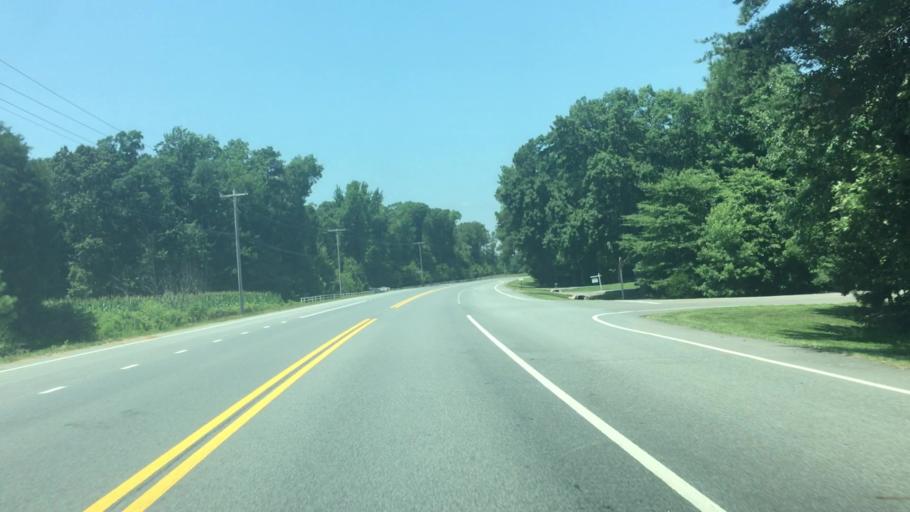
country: US
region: Maryland
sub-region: Saint Mary's County
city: Mechanicsville
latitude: 38.3737
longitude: -76.8101
